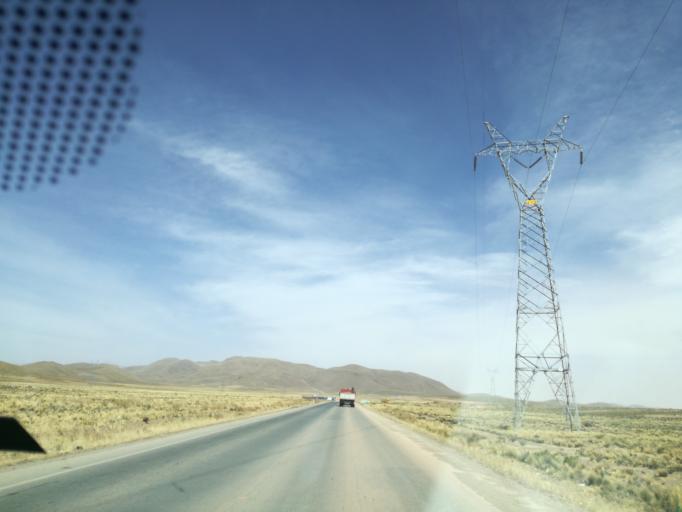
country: BO
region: Oruro
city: Oruro
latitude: -17.8366
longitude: -67.0276
